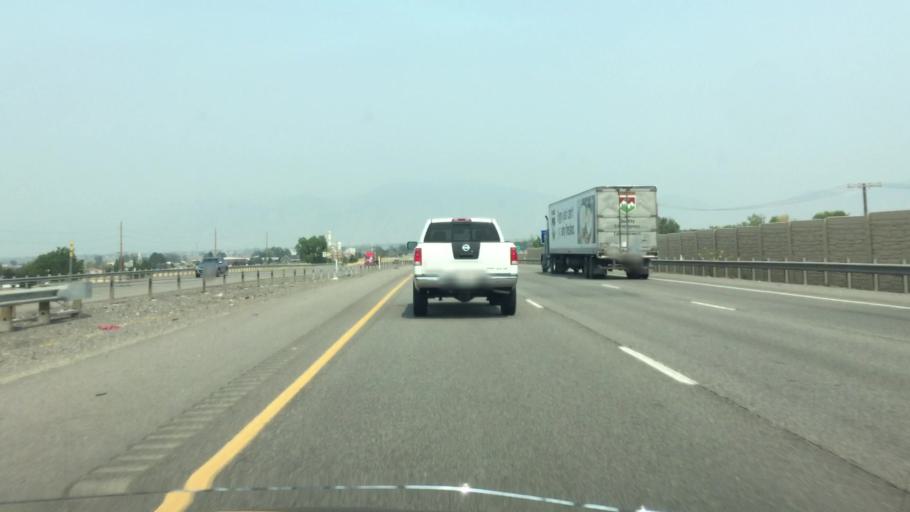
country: US
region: Utah
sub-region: Utah County
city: Payson
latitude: 40.0490
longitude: -111.7394
